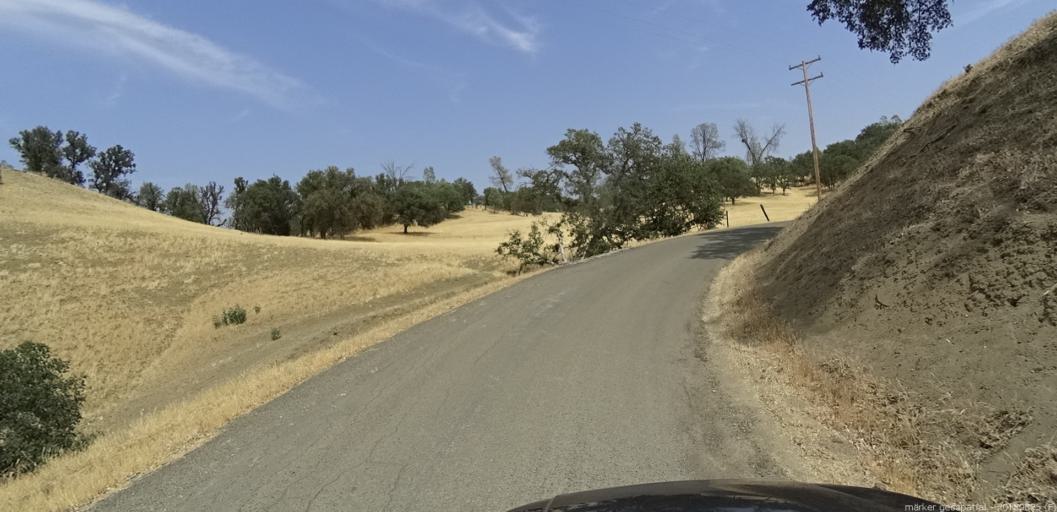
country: US
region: California
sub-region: Fresno County
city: Coalinga
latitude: 36.1837
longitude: -120.6876
